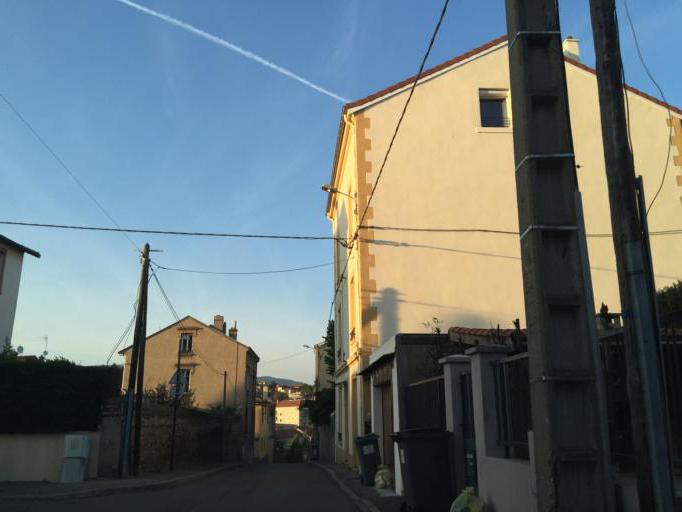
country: FR
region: Rhone-Alpes
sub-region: Departement de la Loire
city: Saint-Chamond
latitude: 45.4733
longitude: 4.5065
